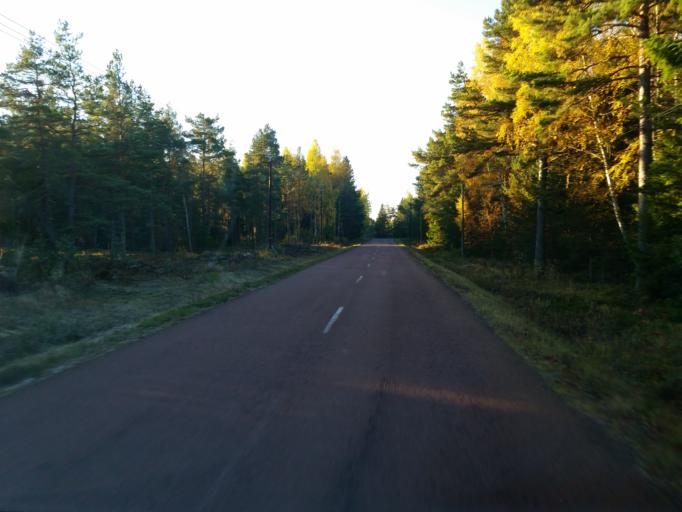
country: AX
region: Alands skaergard
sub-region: Vardoe
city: Vardoe
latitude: 60.3019
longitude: 20.3829
